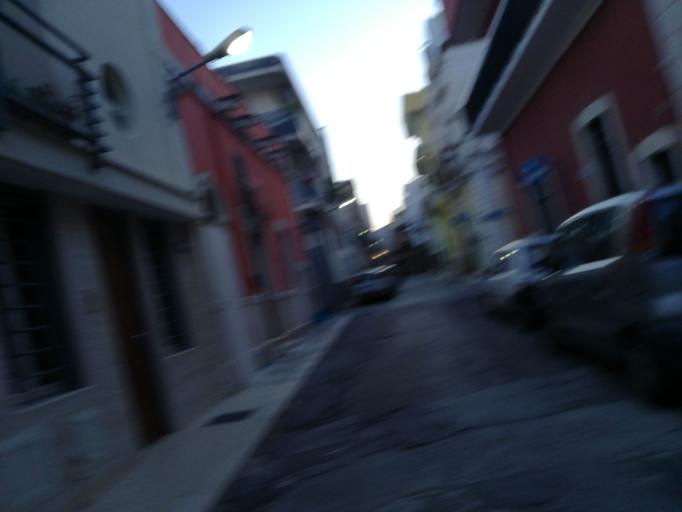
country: IT
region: Apulia
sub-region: Provincia di Bari
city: Triggiano
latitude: 41.0630
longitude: 16.9263
